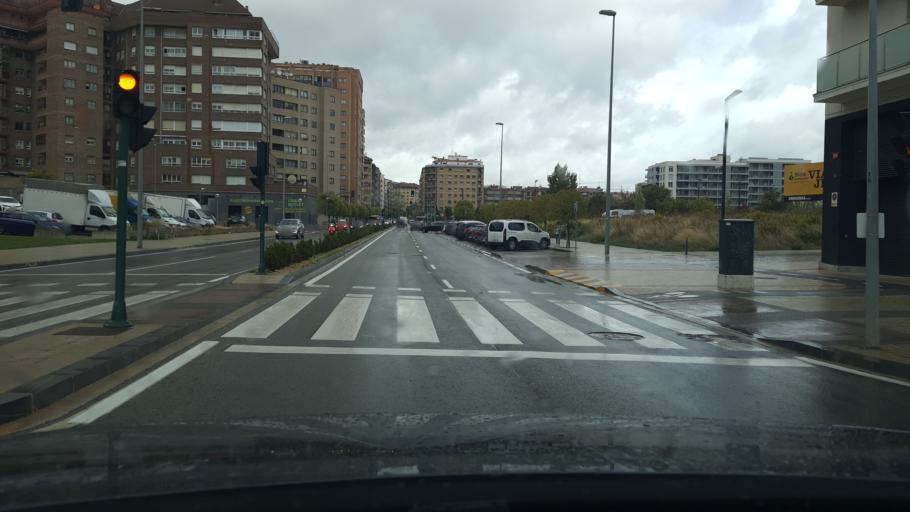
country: ES
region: Navarre
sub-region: Provincia de Navarra
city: Segundo Ensanche
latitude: 42.7998
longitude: -1.6433
